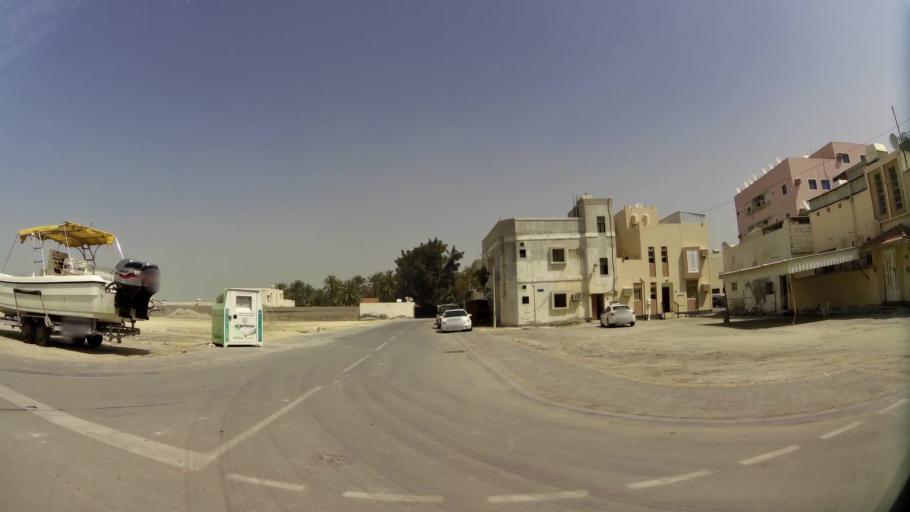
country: BH
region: Manama
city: Jidd Hafs
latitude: 26.2174
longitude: 50.4501
